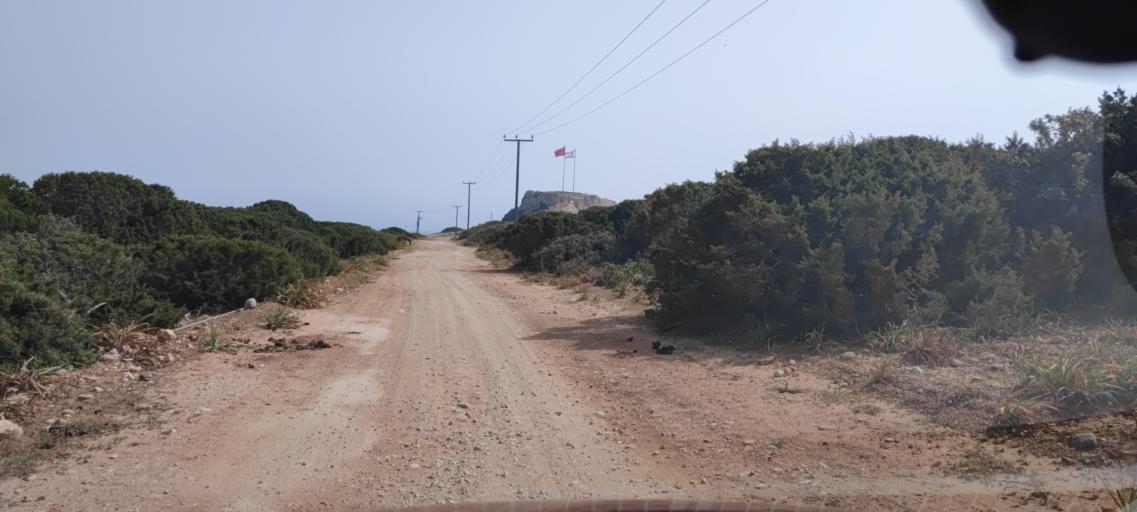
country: CY
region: Ammochostos
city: Rizokarpaso
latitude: 35.6922
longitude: 34.5844
